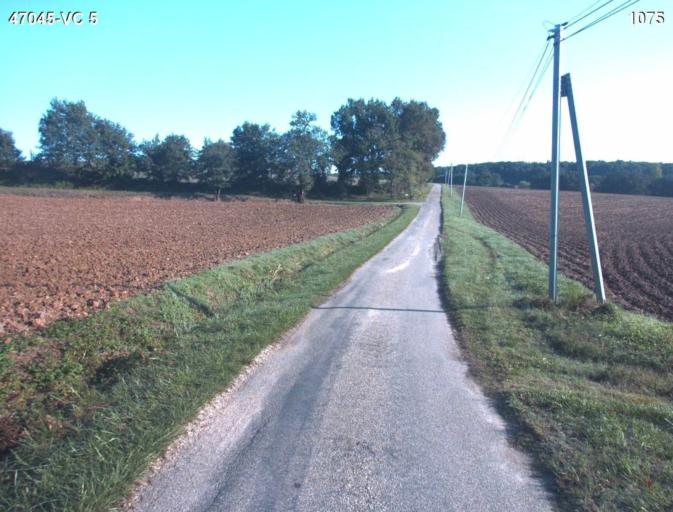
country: FR
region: Aquitaine
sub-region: Departement du Lot-et-Garonne
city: Nerac
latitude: 44.1393
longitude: 0.4047
